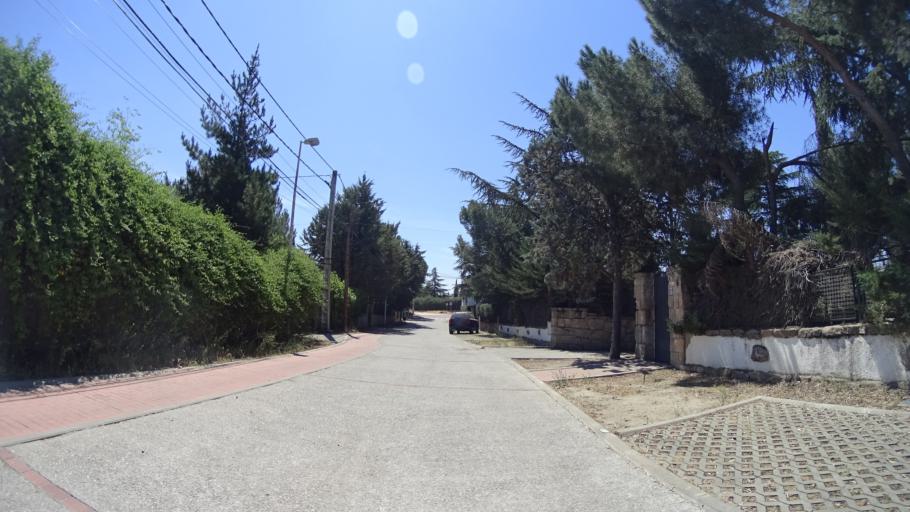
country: ES
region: Madrid
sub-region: Provincia de Madrid
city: Colmenarejo
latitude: 40.5576
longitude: -4.0093
